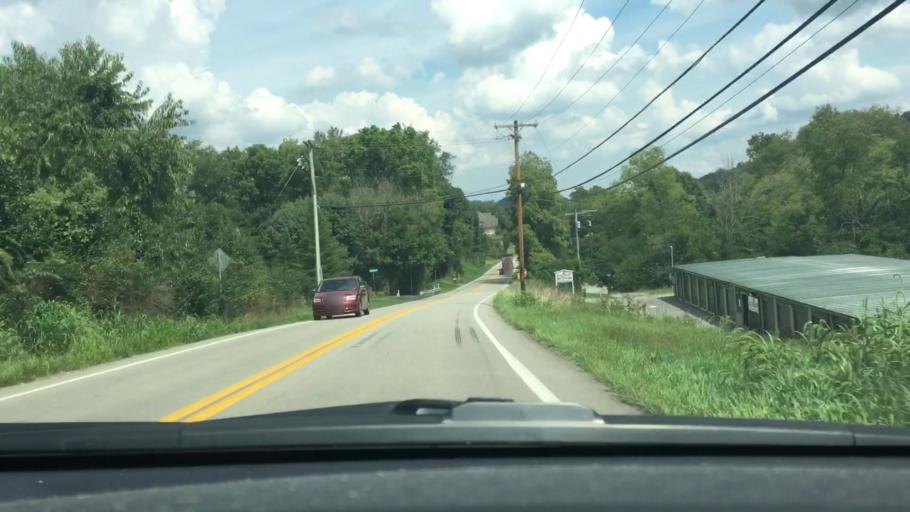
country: US
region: Pennsylvania
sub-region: Washington County
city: McMurray
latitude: 40.2370
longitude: -80.0793
